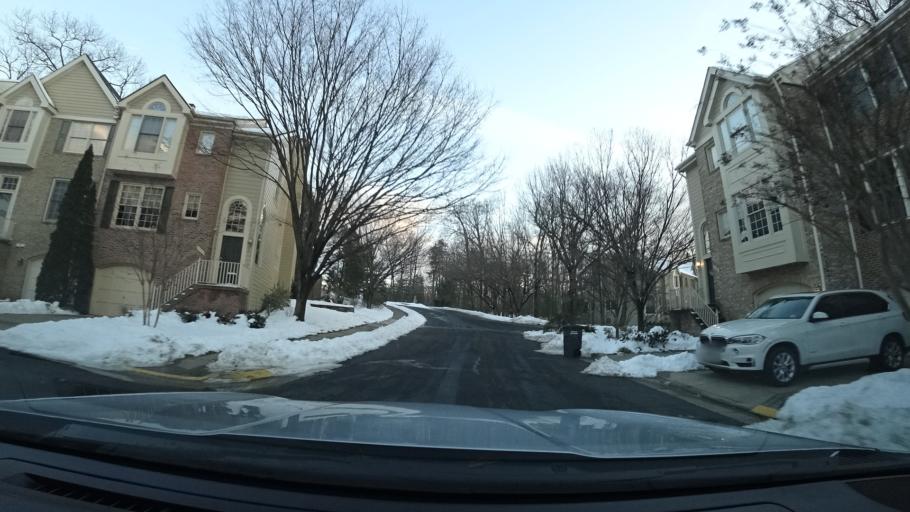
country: US
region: Virginia
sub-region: Fairfax County
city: Reston
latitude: 38.9807
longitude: -77.3396
